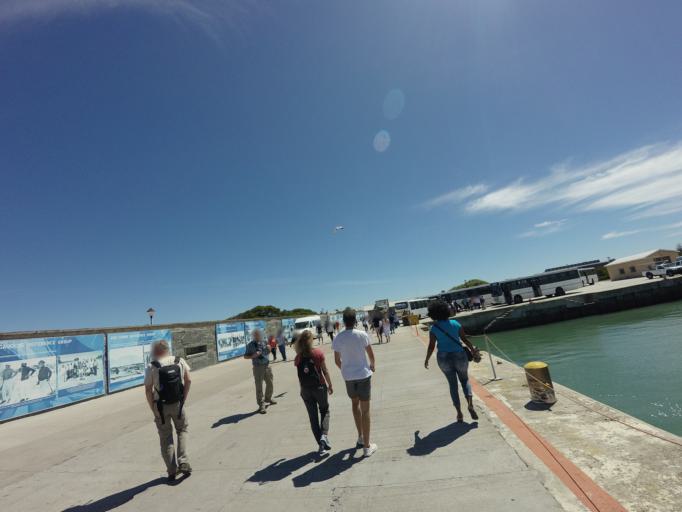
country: ZA
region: Western Cape
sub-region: City of Cape Town
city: Sunset Beach
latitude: -33.7989
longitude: 18.3761
